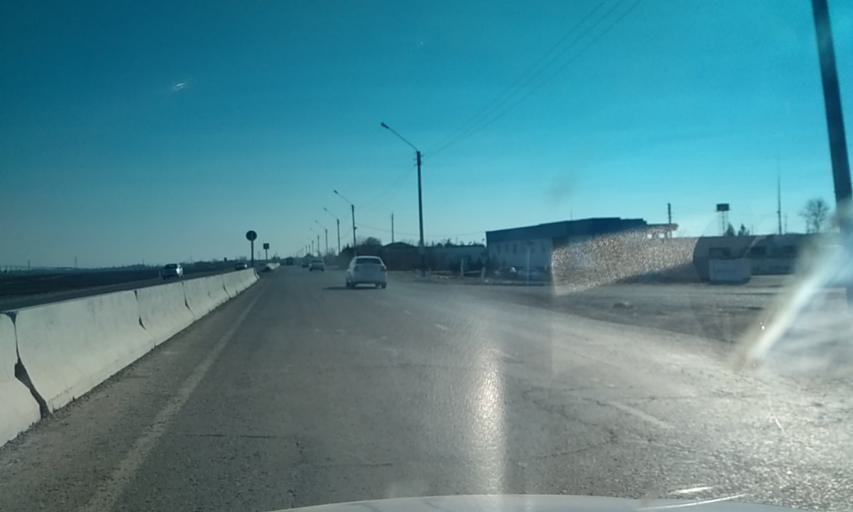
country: UZ
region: Sirdaryo
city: Guliston
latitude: 40.4680
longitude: 68.7719
